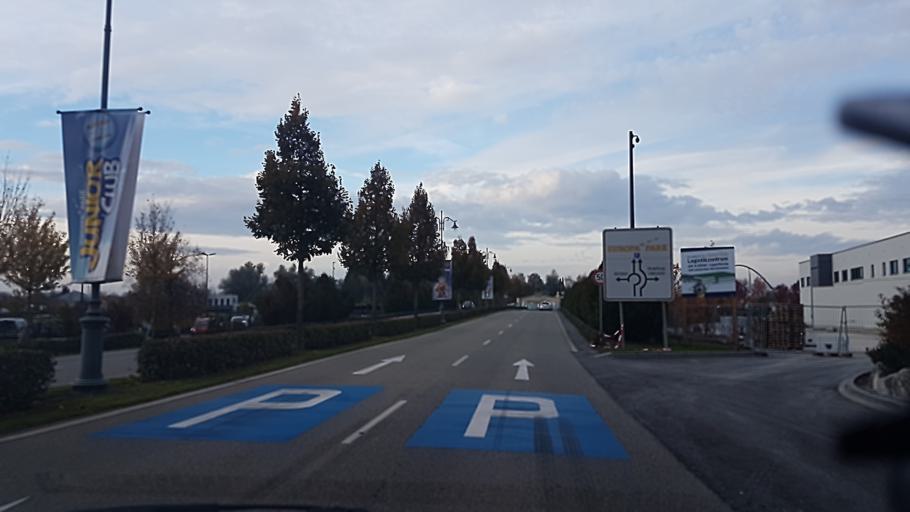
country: DE
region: Baden-Wuerttemberg
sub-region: Freiburg Region
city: Rust
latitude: 48.2626
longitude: 7.7172
